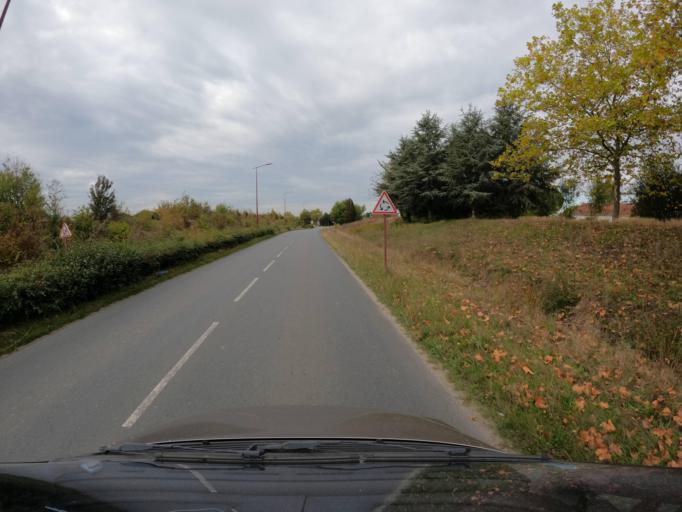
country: FR
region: Pays de la Loire
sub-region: Departement de la Loire-Atlantique
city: Clisson
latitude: 47.0871
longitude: -1.2946
